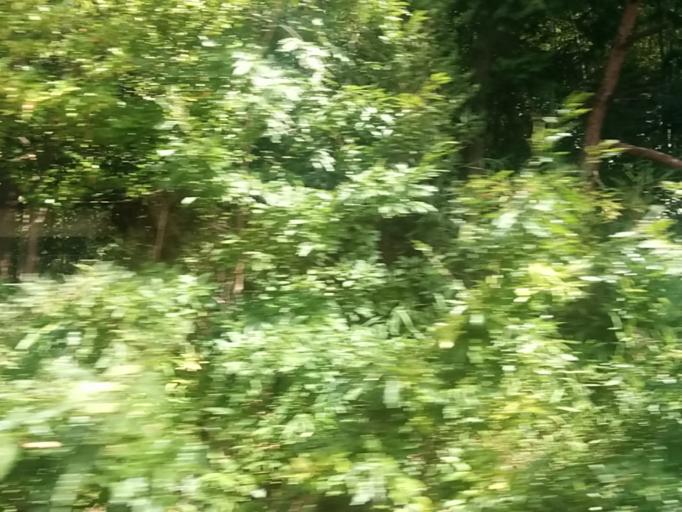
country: JP
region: Nara
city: Nara-shi
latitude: 34.6757
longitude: 135.7833
